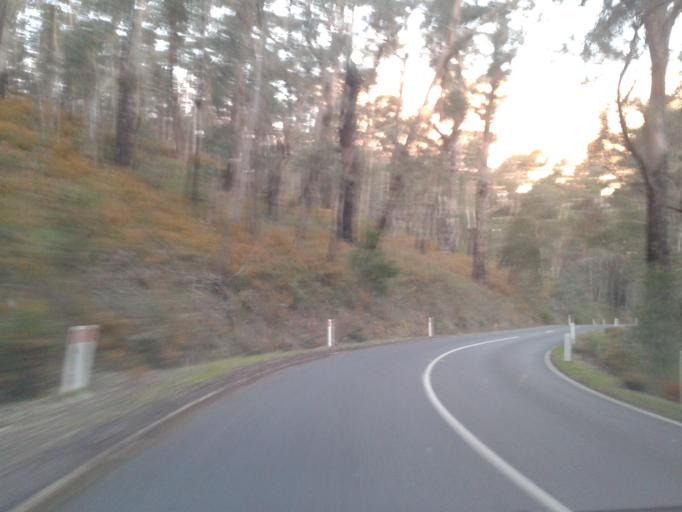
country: AU
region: Victoria
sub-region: Northern Grampians
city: Stawell
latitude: -37.1482
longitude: 142.4721
